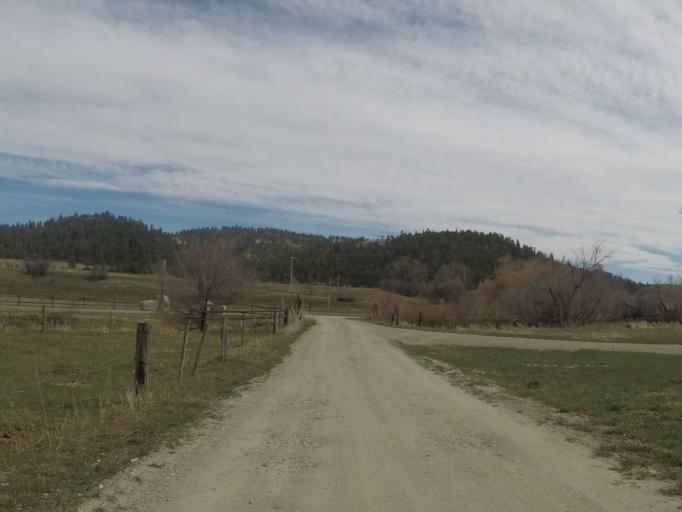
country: US
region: Montana
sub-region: Stillwater County
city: Columbus
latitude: 45.5816
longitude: -109.3296
